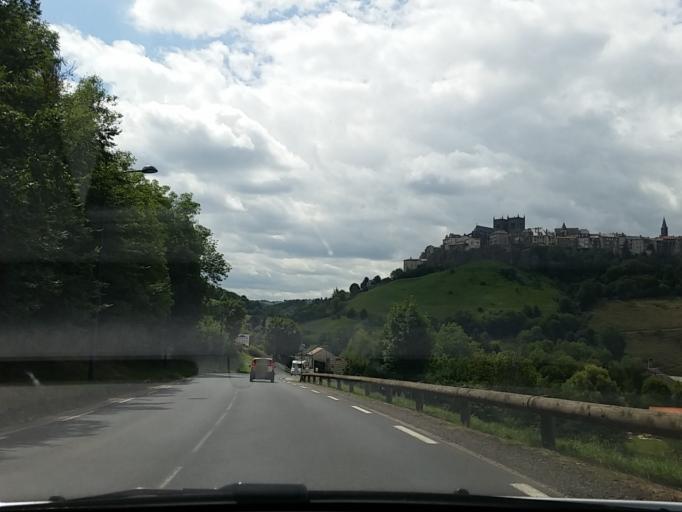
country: FR
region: Auvergne
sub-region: Departement du Cantal
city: Saint-Flour
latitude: 45.0377
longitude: 3.1018
